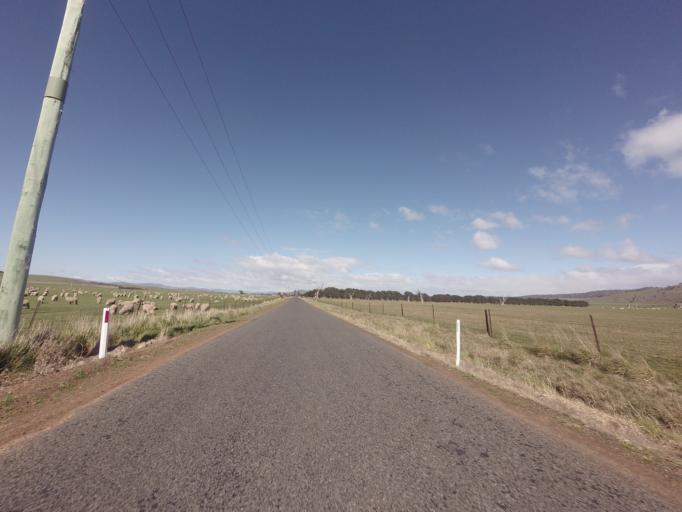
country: AU
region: Tasmania
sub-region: Northern Midlands
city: Evandale
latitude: -41.9905
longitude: 147.4524
